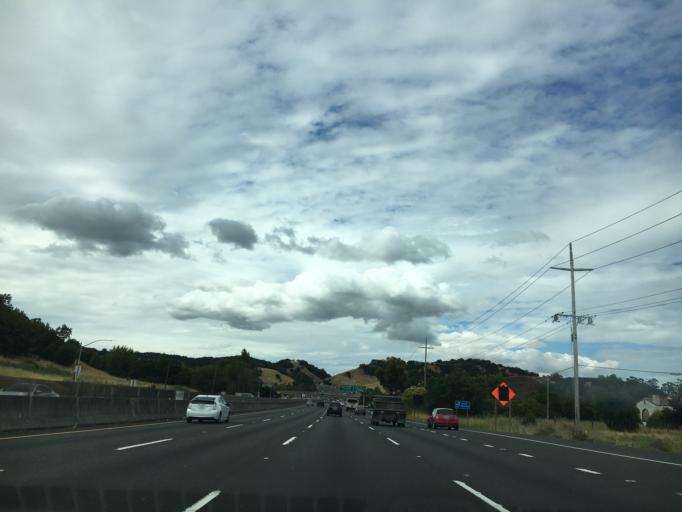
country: US
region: California
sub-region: Marin County
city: Santa Venetia
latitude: 38.0278
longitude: -122.5374
